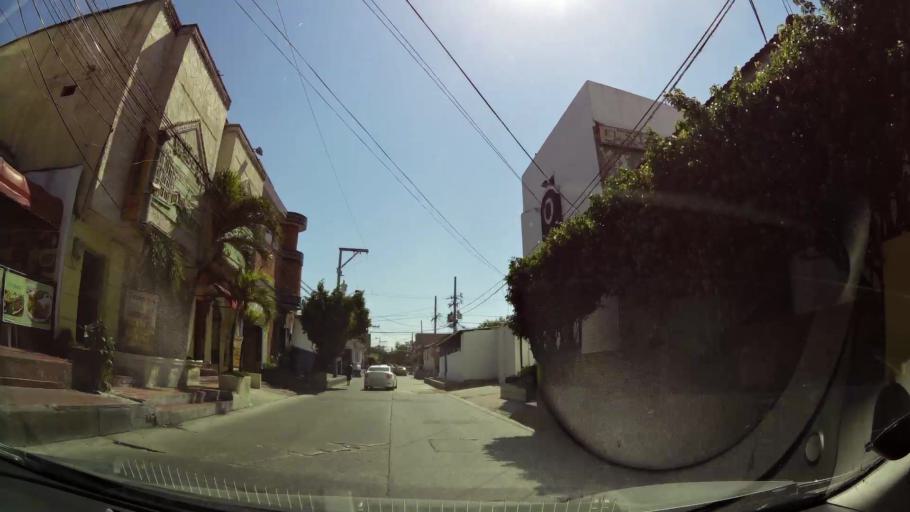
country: CO
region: Atlantico
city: Barranquilla
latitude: 10.9805
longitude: -74.7858
